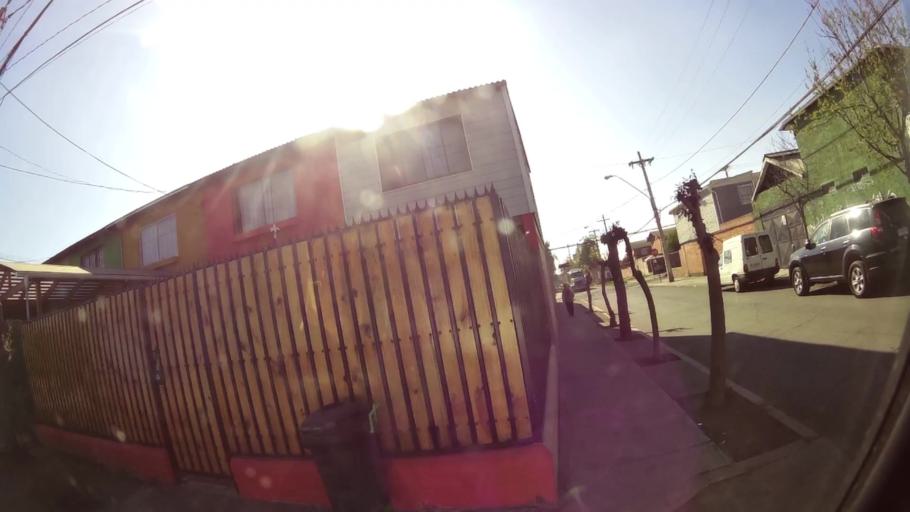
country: CL
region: Santiago Metropolitan
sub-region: Provincia de Santiago
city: Lo Prado
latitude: -33.4891
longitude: -70.7695
